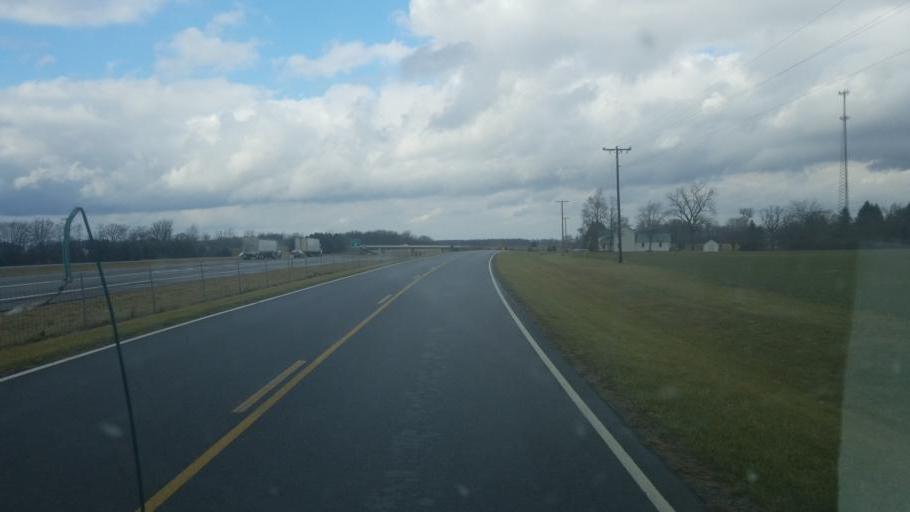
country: US
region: Ohio
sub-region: Wyandot County
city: Upper Sandusky
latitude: 40.7782
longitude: -83.2428
